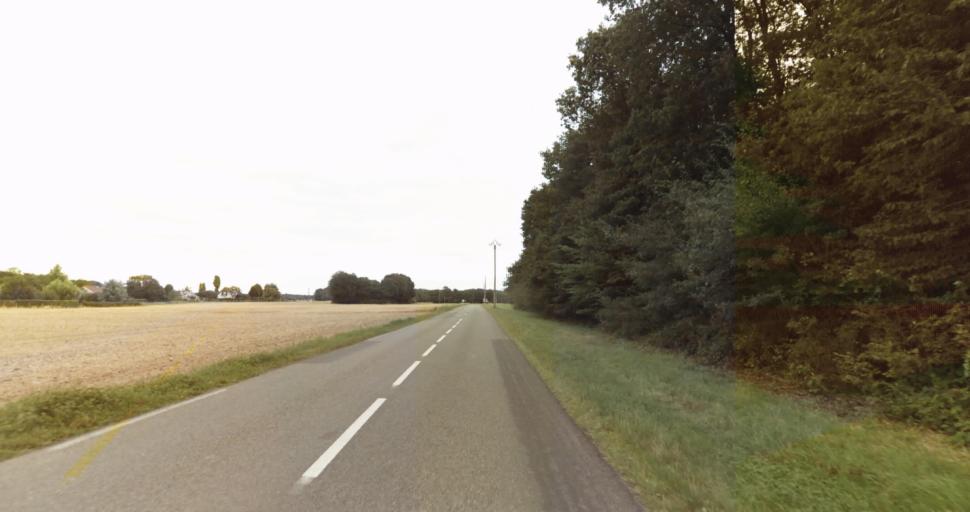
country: FR
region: Haute-Normandie
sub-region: Departement de l'Eure
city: Gravigny
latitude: 48.9837
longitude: 1.2620
